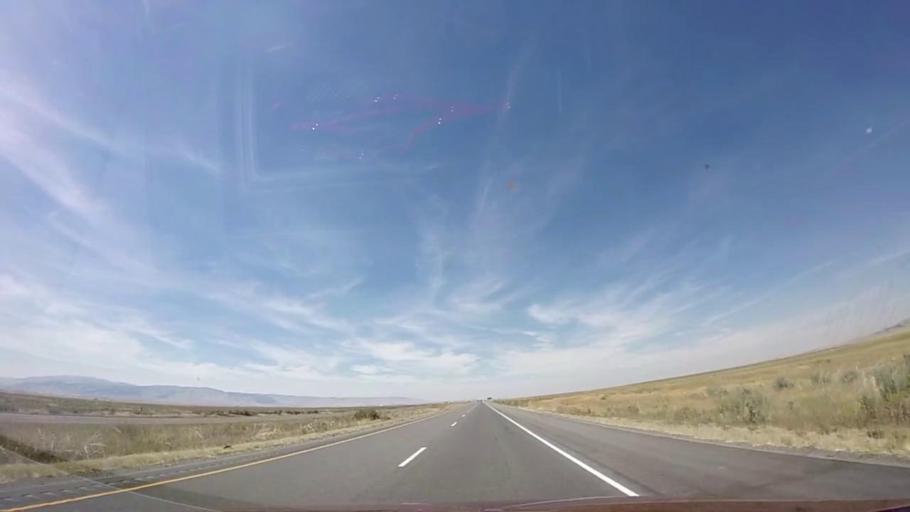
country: US
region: Idaho
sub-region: Power County
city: American Falls
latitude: 42.3018
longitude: -113.1805
